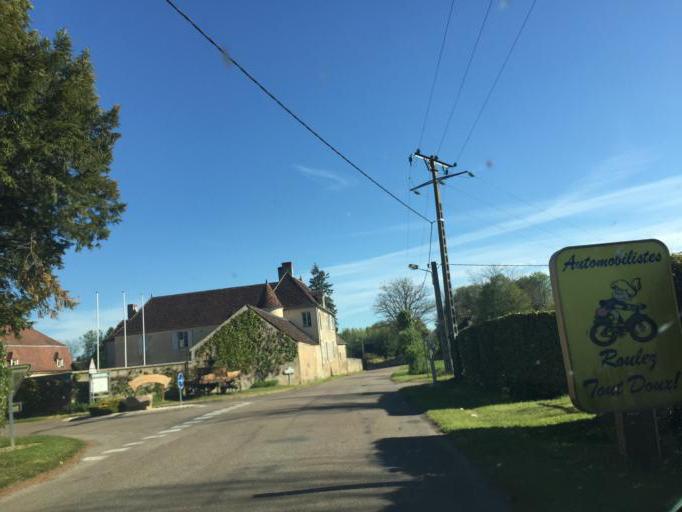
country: FR
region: Bourgogne
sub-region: Departement de la Nievre
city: Clamecy
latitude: 47.5074
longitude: 3.5163
